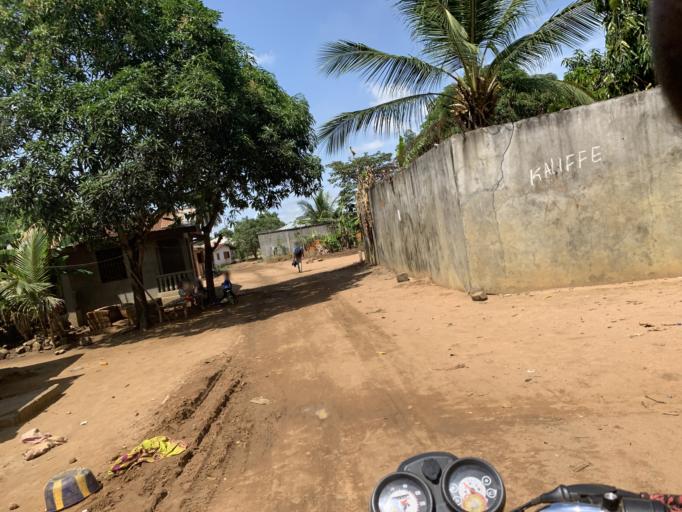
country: SL
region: Western Area
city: Waterloo
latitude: 8.3403
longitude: -13.0513
